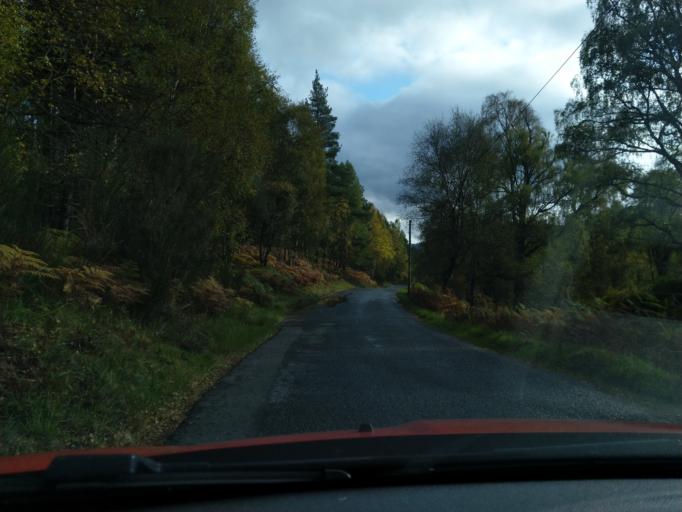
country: GB
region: Scotland
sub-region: Perth and Kinross
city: Aberfeldy
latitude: 56.7090
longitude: -4.0665
